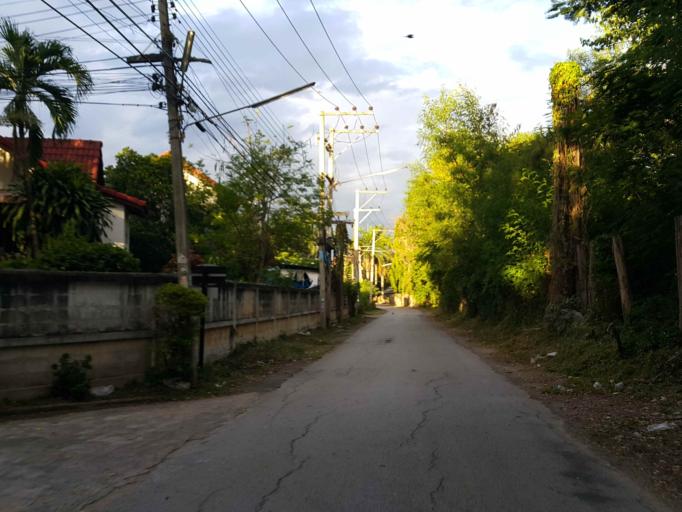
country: TH
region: Chiang Mai
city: Chiang Mai
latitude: 18.8096
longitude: 99.0226
